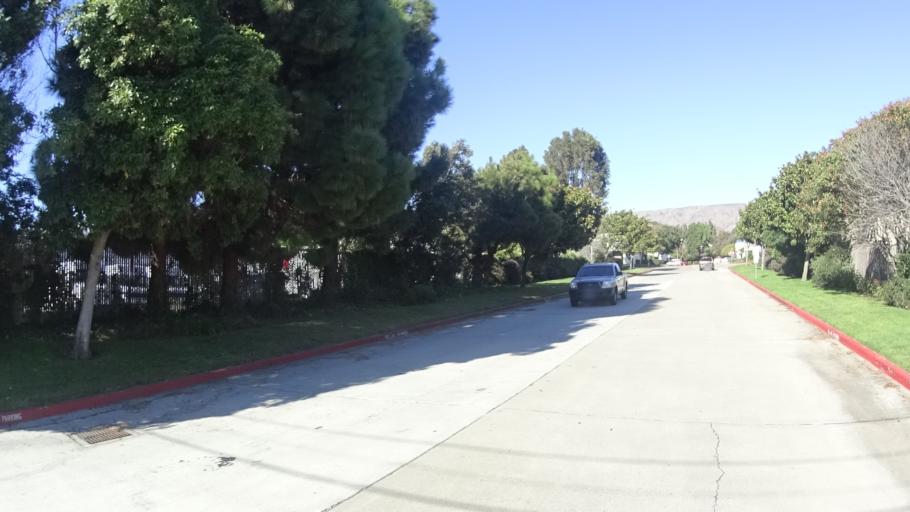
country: US
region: California
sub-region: San Mateo County
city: South San Francisco
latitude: 37.6511
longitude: -122.4151
